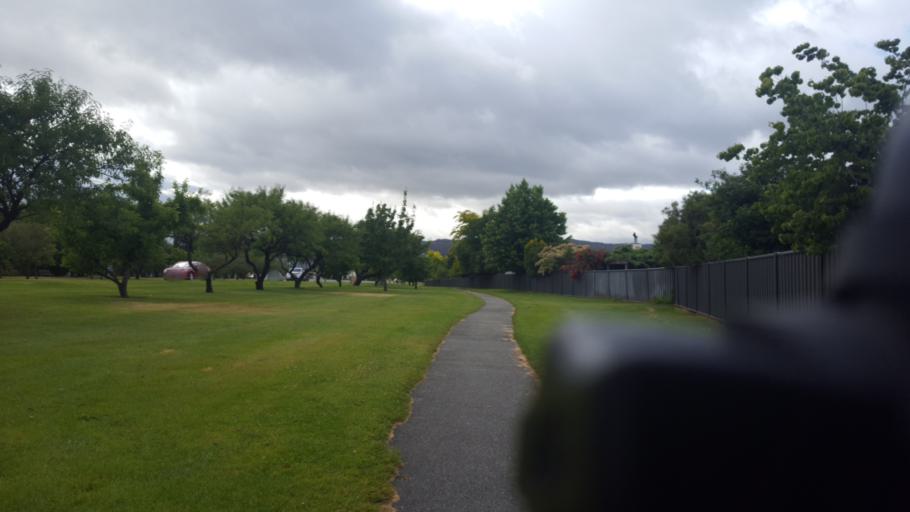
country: NZ
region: Otago
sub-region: Queenstown-Lakes District
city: Wanaka
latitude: -45.2447
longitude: 169.3791
